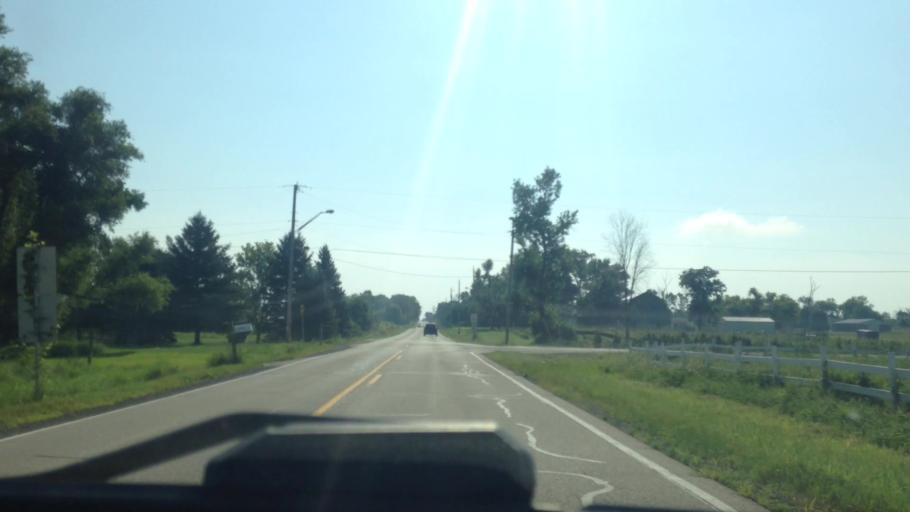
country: US
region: Wisconsin
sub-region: Waukesha County
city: Sussex
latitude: 43.1627
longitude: -88.2239
